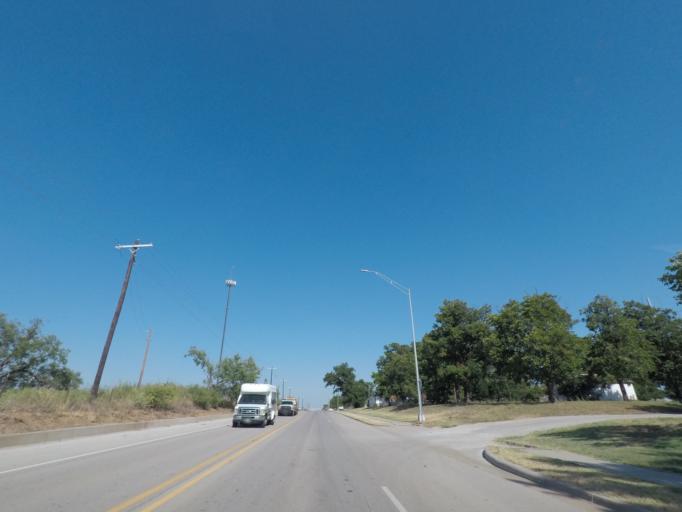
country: US
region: Texas
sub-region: Baylor County
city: Seymour
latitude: 33.5961
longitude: -99.2509
